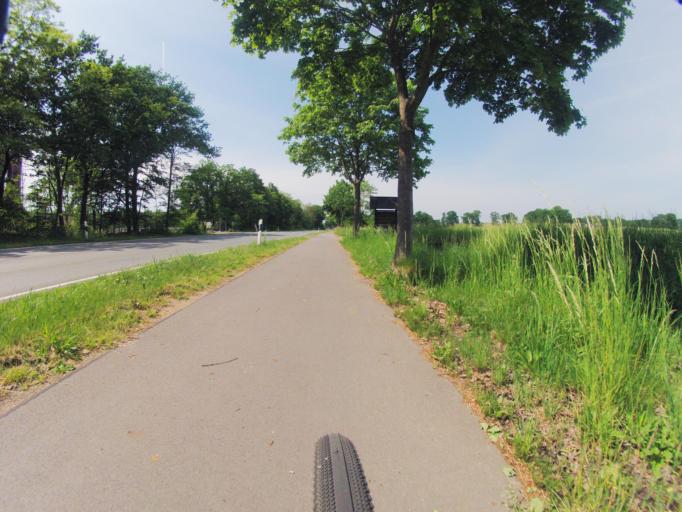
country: DE
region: North Rhine-Westphalia
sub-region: Regierungsbezirk Munster
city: Birgte
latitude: 52.2933
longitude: 7.6663
